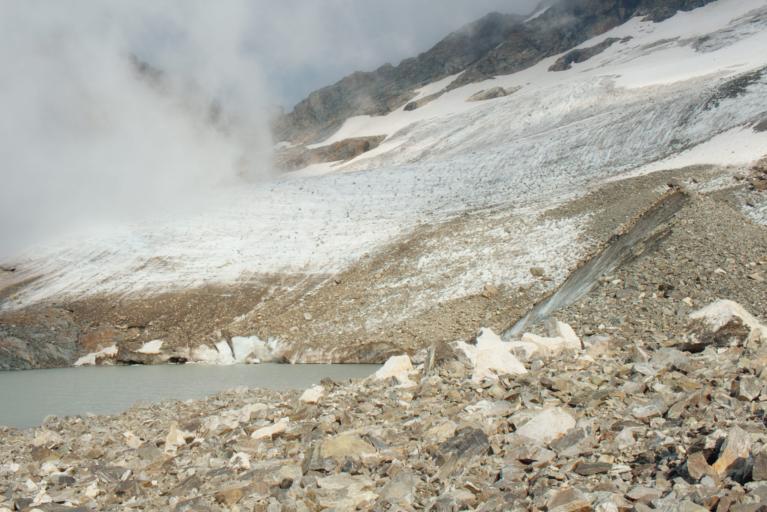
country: RU
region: Karachayevo-Cherkesiya
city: Nizhniy Arkhyz
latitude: 43.4267
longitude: 41.2549
